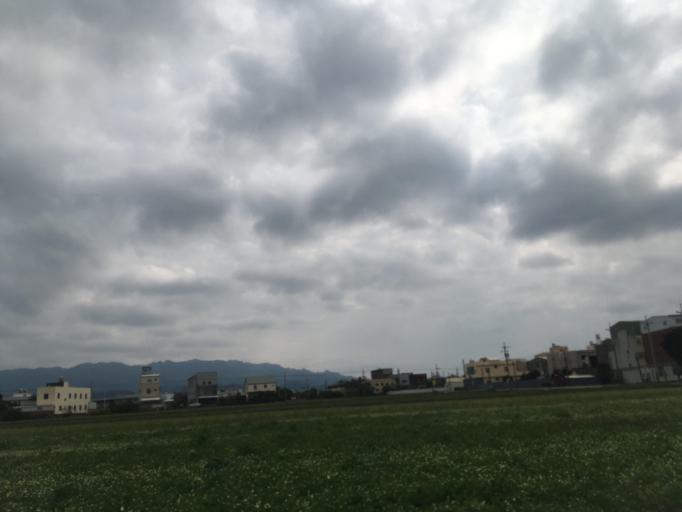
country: TW
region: Taiwan
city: Fengyuan
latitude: 24.4074
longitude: 120.6750
